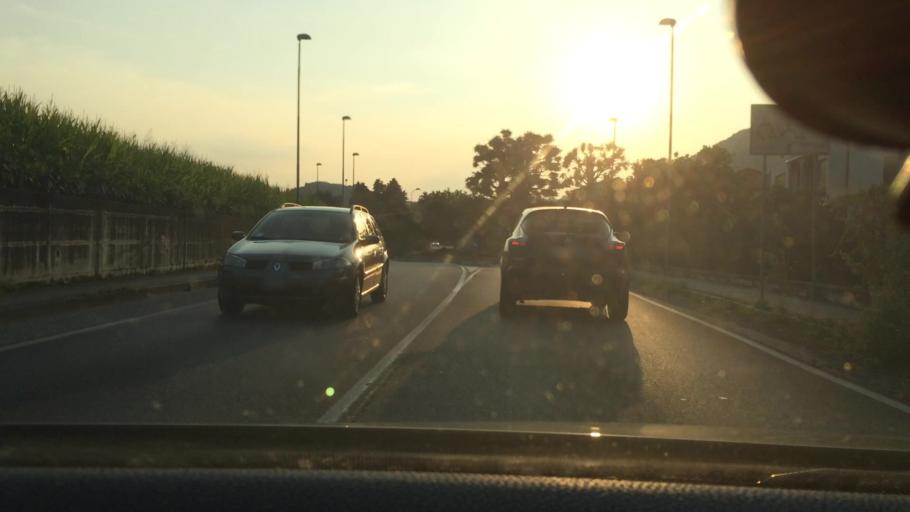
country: IT
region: Lombardy
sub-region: Provincia di Lecco
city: Brivio
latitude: 45.7344
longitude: 9.4283
